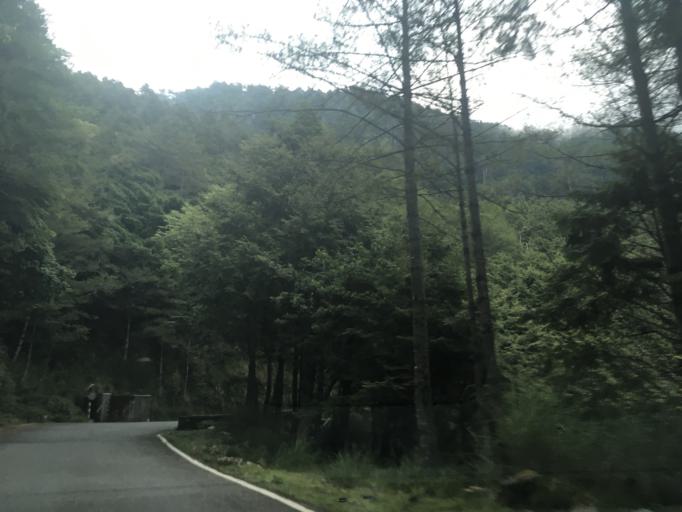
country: TW
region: Taiwan
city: Fengyuan
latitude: 24.2636
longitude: 121.0144
